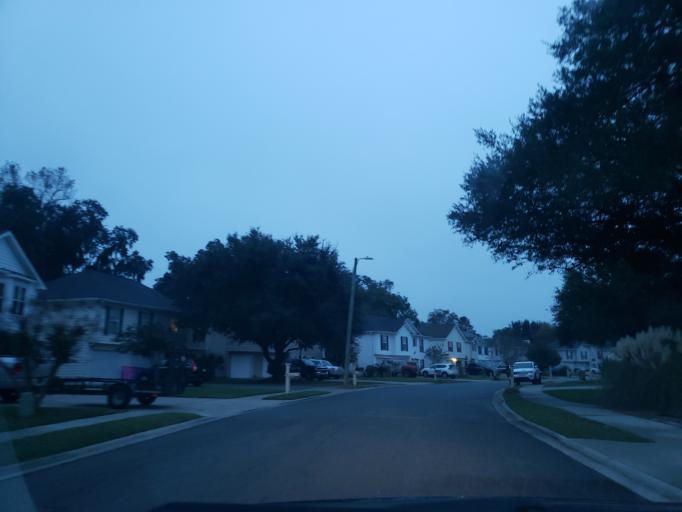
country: US
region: Georgia
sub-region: Chatham County
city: Wilmington Island
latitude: 32.0231
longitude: -80.9597
